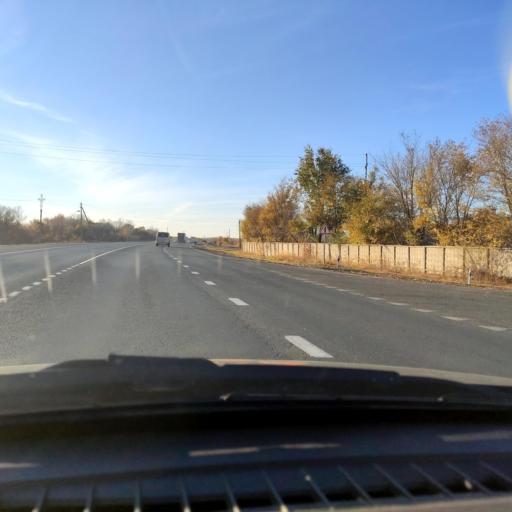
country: RU
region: Samara
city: Varlamovo
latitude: 53.1920
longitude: 48.3404
